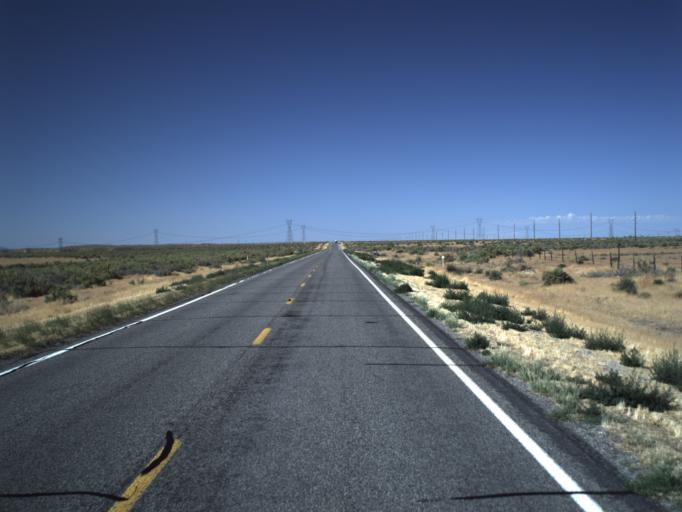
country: US
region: Utah
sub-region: Millard County
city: Delta
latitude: 39.5033
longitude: -112.3891
